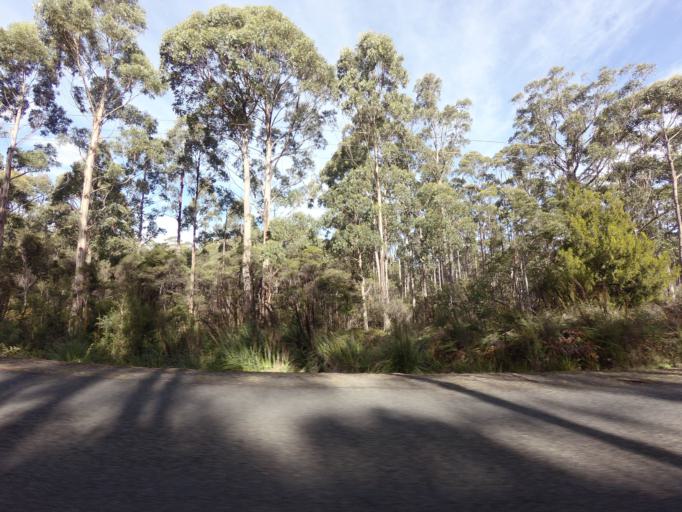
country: AU
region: Tasmania
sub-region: Clarence
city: Sandford
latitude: -43.1306
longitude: 147.7834
